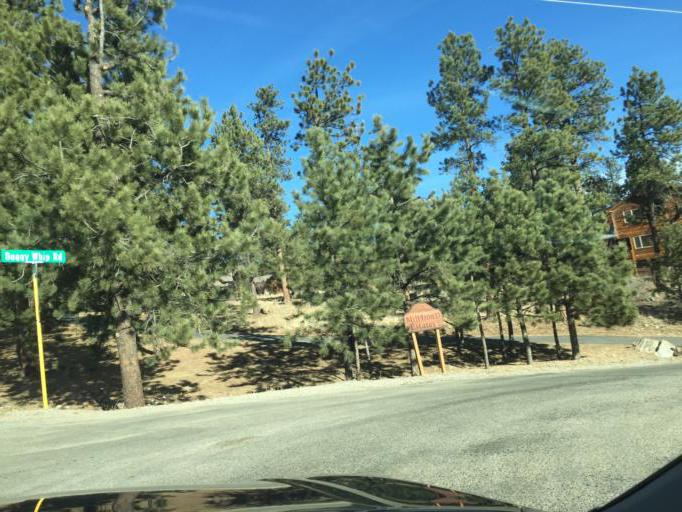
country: US
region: Colorado
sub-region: Jefferson County
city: Evergreen
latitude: 39.4427
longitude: -105.4596
